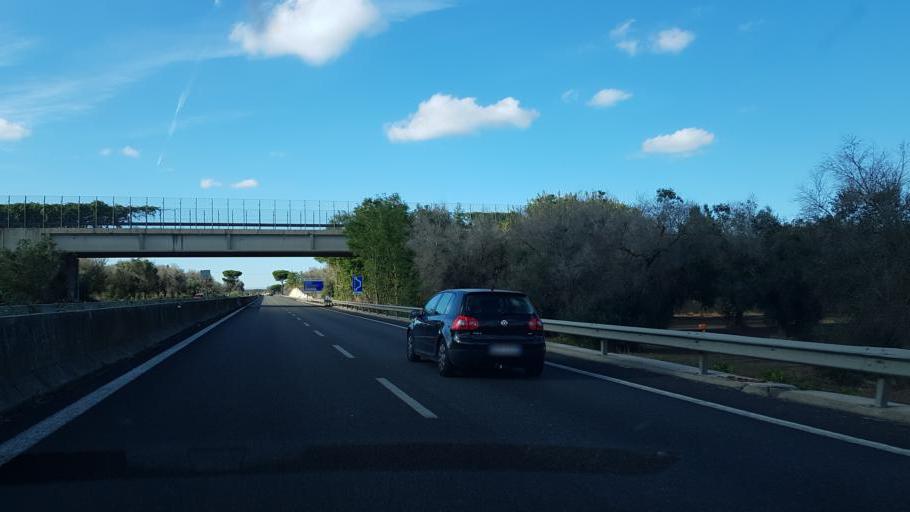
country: IT
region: Apulia
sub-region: Provincia di Brindisi
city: Torchiarolo
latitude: 40.4558
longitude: 18.0634
